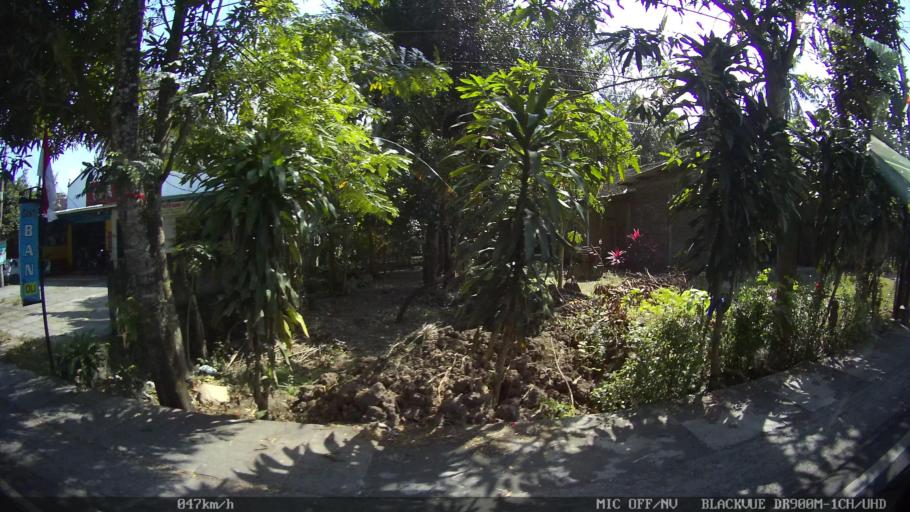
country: ID
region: Daerah Istimewa Yogyakarta
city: Srandakan
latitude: -7.9397
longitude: 110.2270
